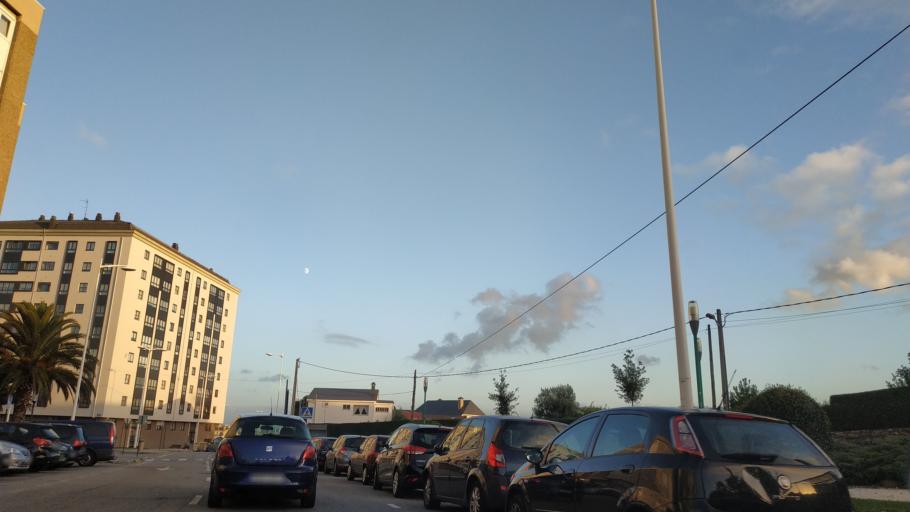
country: ES
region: Galicia
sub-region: Provincia da Coruna
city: A Coruna
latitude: 43.3590
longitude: -8.4261
